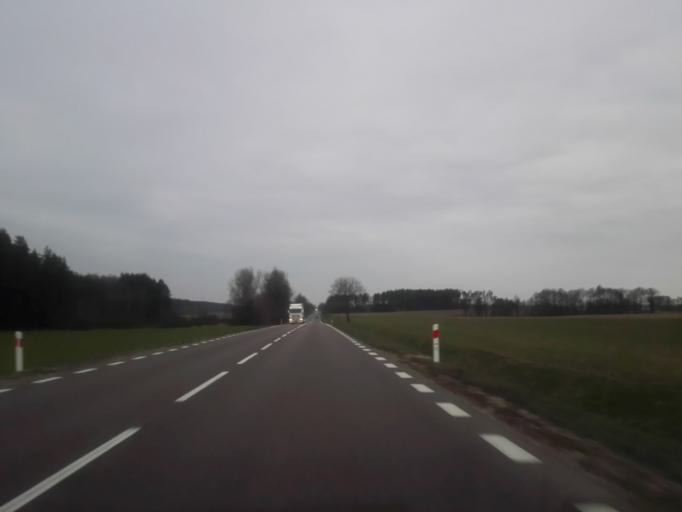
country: PL
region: Podlasie
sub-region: Powiat kolnenski
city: Stawiski
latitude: 53.4756
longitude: 22.2096
